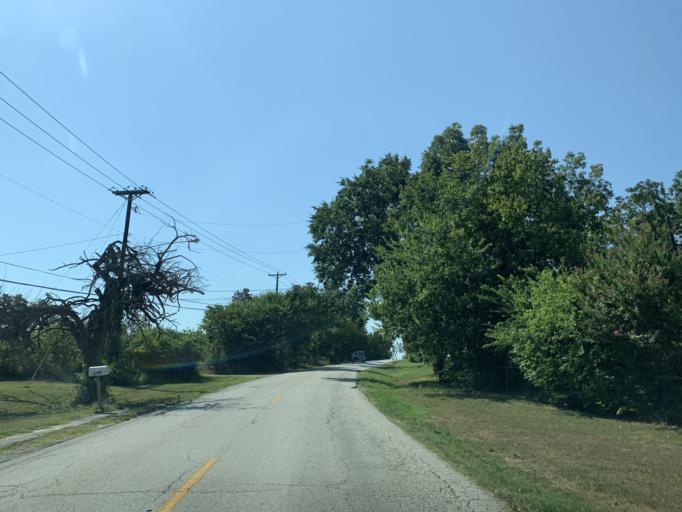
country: US
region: Texas
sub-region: Dallas County
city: Hutchins
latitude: 32.6724
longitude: -96.7463
